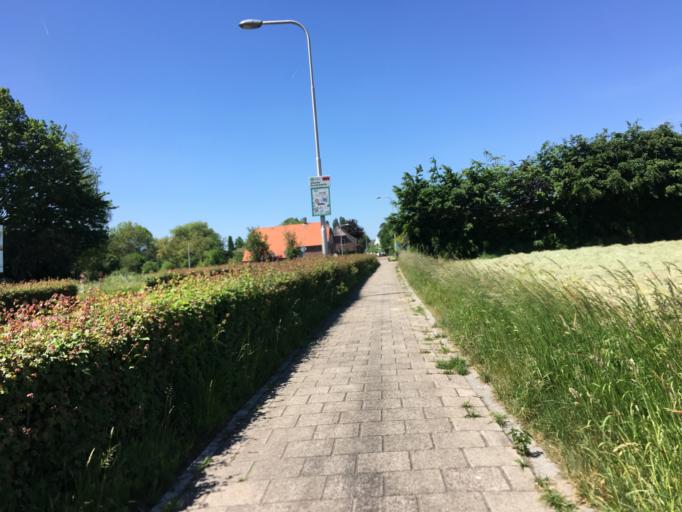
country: NL
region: North Brabant
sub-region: Gemeente Heusden
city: Heusden
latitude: 51.7308
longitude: 5.1612
